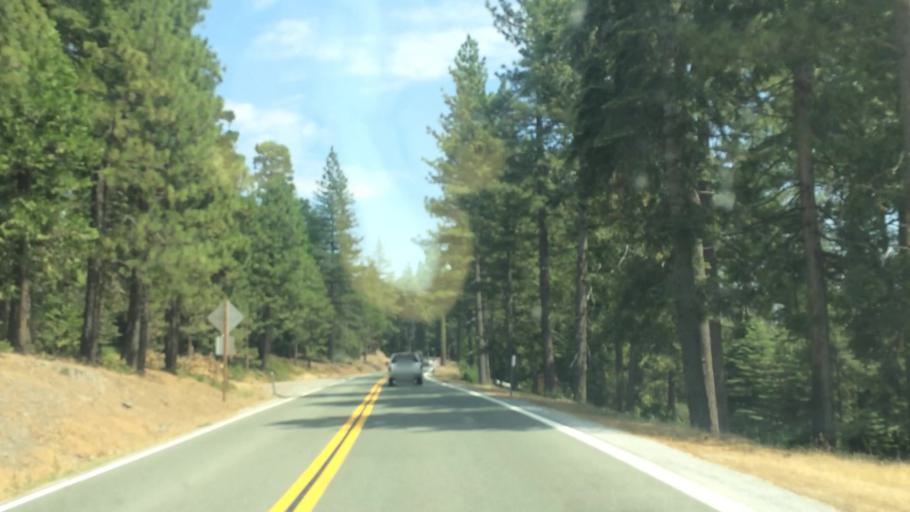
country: US
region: California
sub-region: Amador County
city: Pioneer
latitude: 38.5277
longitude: -120.4374
